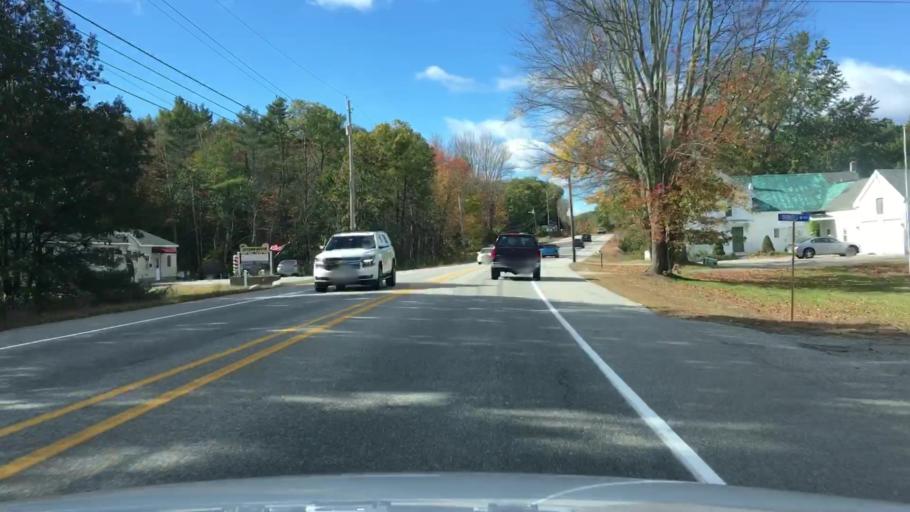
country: US
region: Maine
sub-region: York County
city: West Kennebunk
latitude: 43.4786
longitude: -70.5883
